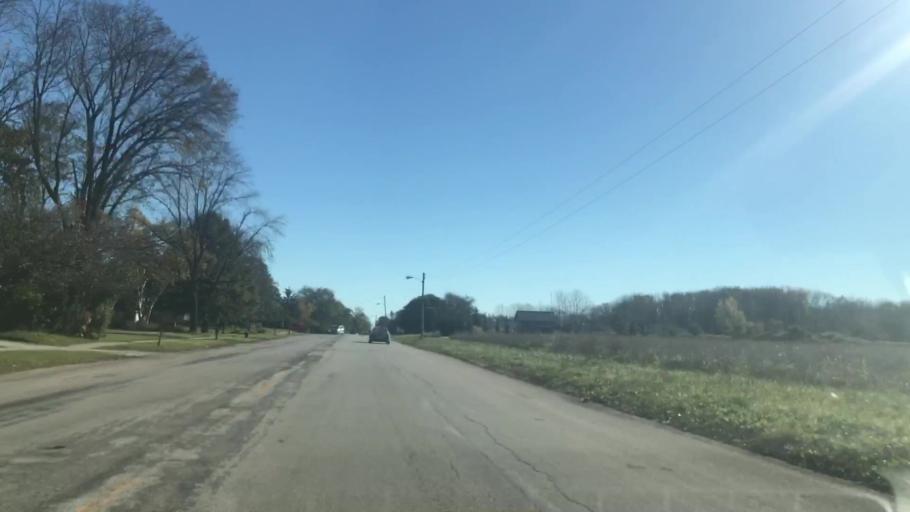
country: US
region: Wisconsin
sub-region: Waukesha County
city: Menomonee Falls
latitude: 43.1702
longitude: -88.1307
